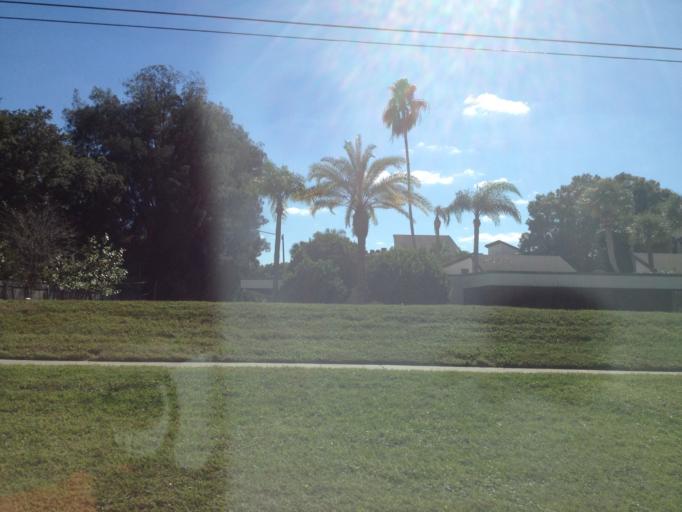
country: US
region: Florida
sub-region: Pinellas County
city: South Highpoint
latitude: 27.9385
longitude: -82.7445
